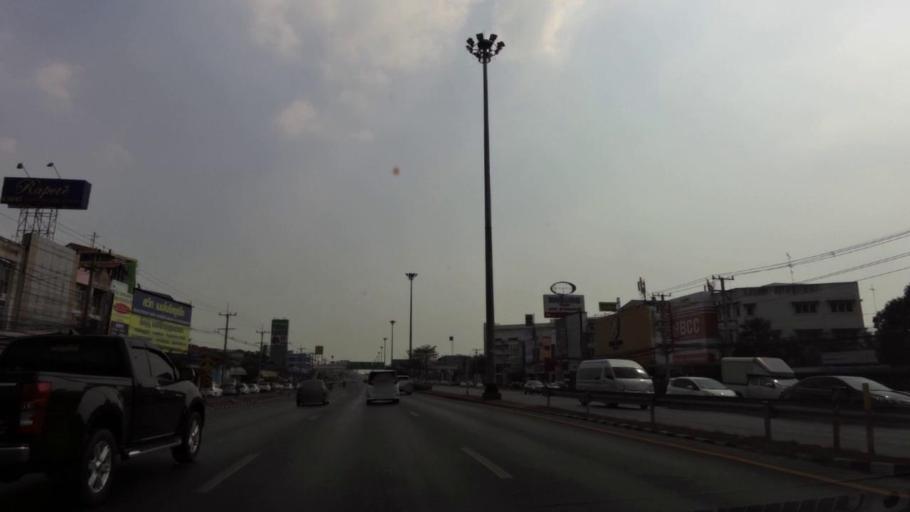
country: TH
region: Phra Nakhon Si Ayutthaya
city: Phra Nakhon Si Ayutthaya
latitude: 14.3528
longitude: 100.6011
